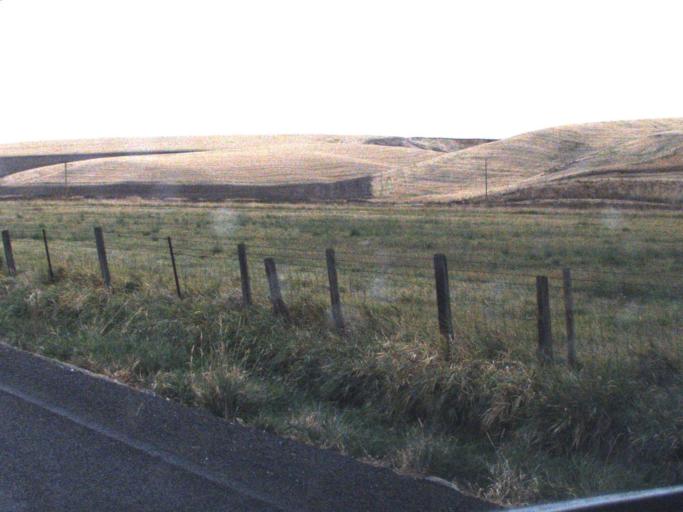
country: US
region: Washington
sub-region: Whitman County
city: Colfax
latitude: 46.8051
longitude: -117.5700
